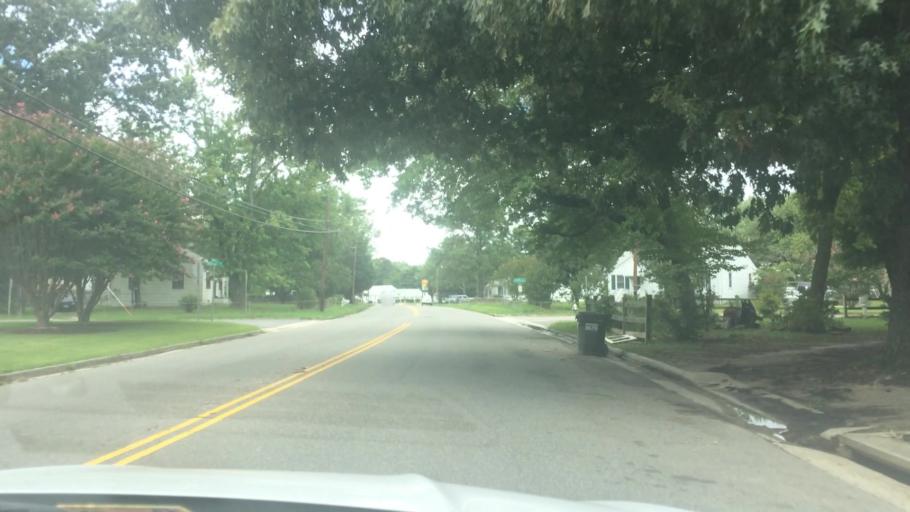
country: US
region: Virginia
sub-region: City of Williamsburg
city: Williamsburg
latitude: 37.2619
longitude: -76.6647
